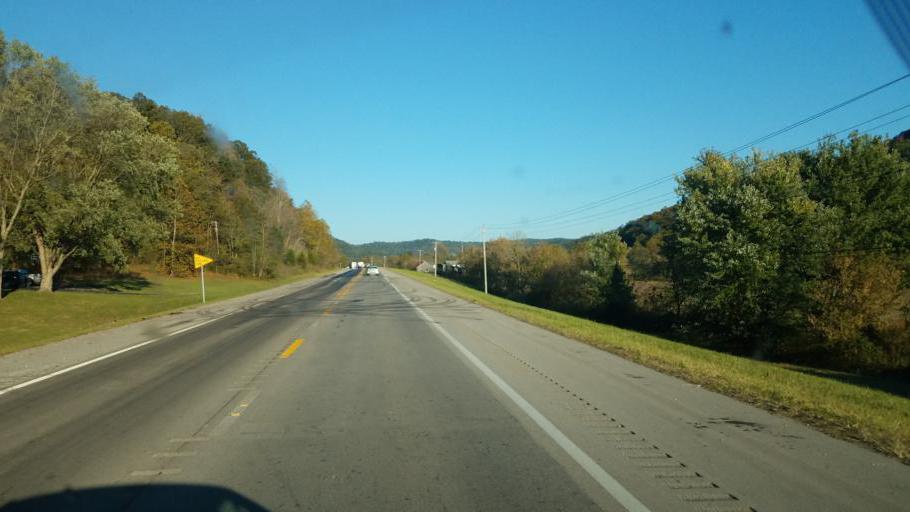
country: US
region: Kentucky
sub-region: Lewis County
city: Vanceburg
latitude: 38.5865
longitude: -83.3917
